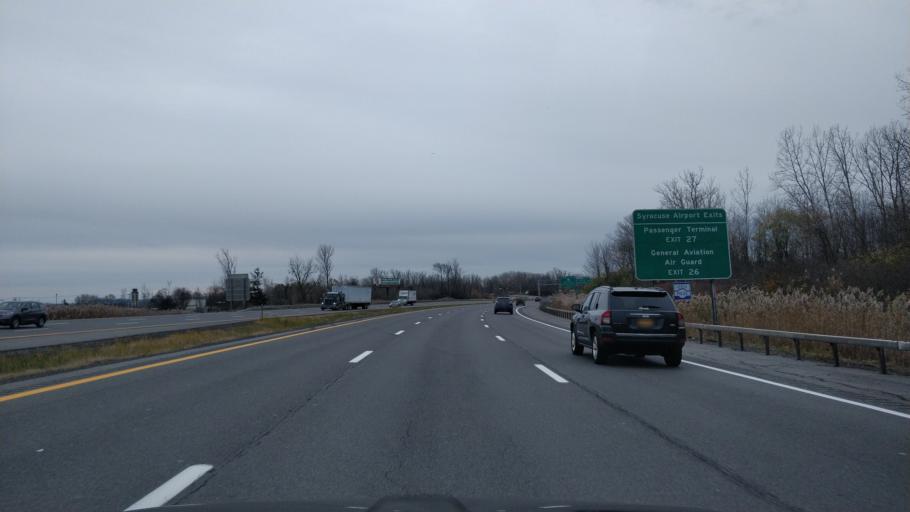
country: US
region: New York
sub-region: Onondaga County
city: North Syracuse
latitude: 43.1298
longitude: -76.1199
